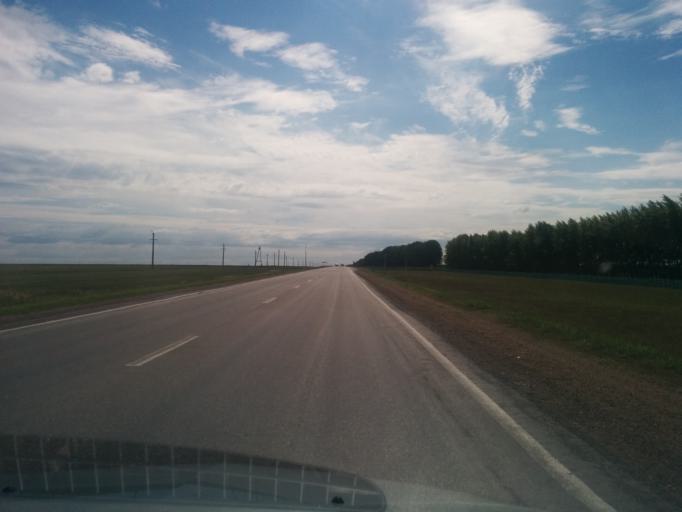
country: RU
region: Bashkortostan
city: Karmaskaly
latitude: 54.4221
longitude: 56.0407
